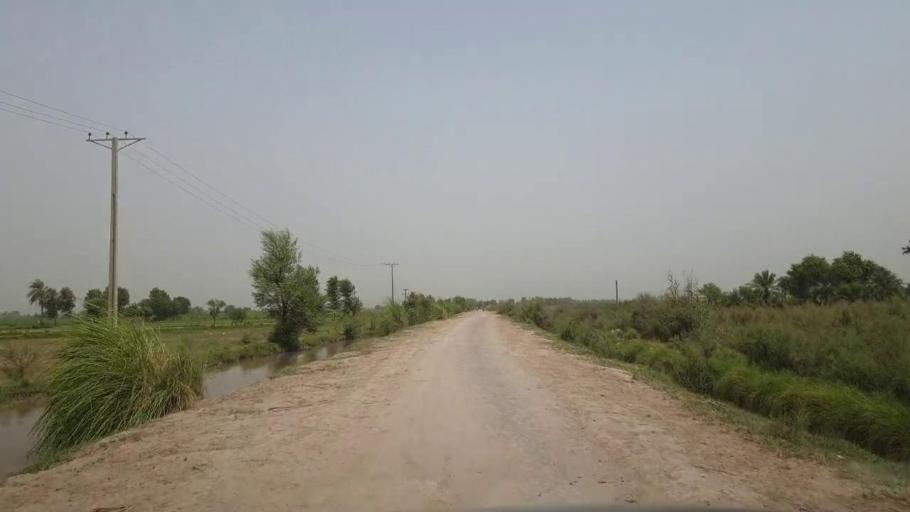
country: PK
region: Sindh
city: Gambat
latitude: 27.4470
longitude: 68.4443
